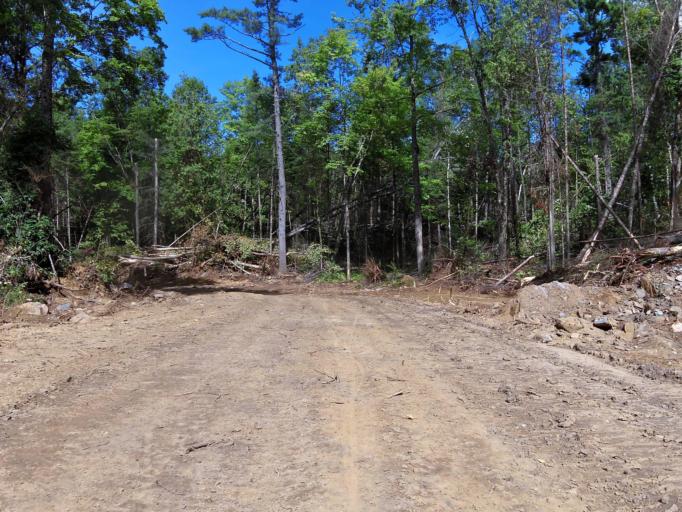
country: CA
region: Ontario
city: Renfrew
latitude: 45.1072
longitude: -76.7176
